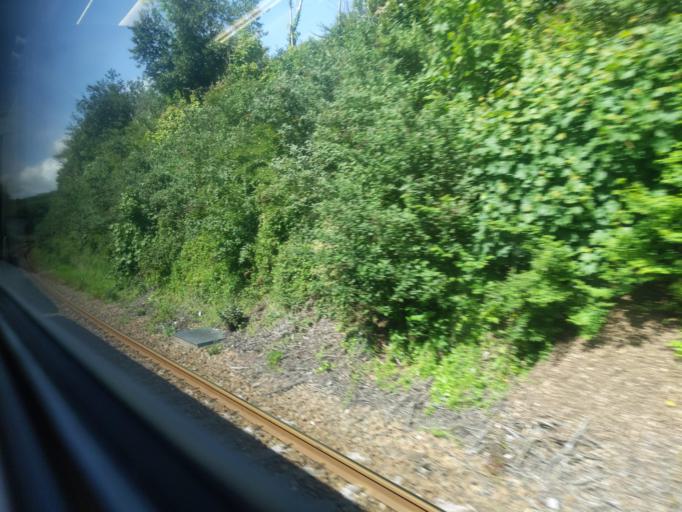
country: GB
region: England
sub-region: Cornwall
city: St Austell
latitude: 50.3407
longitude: -4.7942
